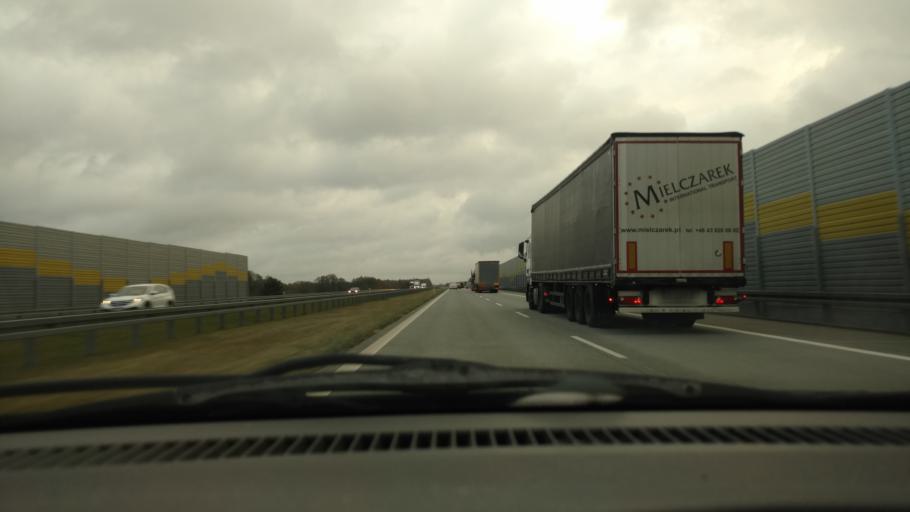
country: PL
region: Lodz Voivodeship
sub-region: Powiat pabianicki
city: Ksawerow
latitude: 51.6302
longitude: 19.4117
